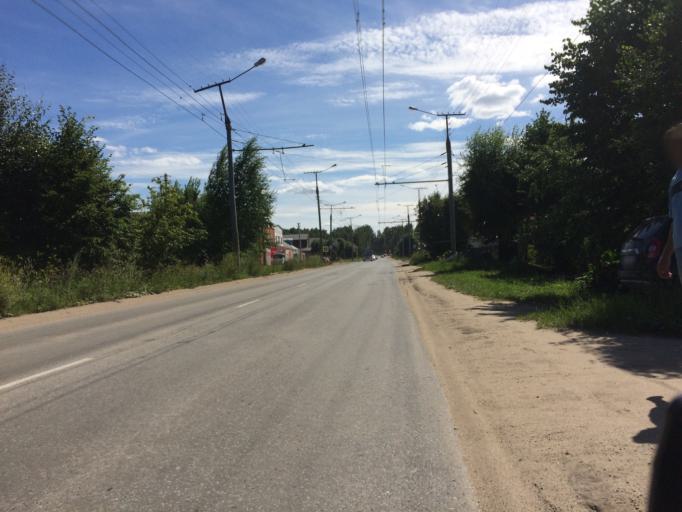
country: RU
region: Mariy-El
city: Yoshkar-Ola
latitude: 56.6449
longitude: 47.9542
